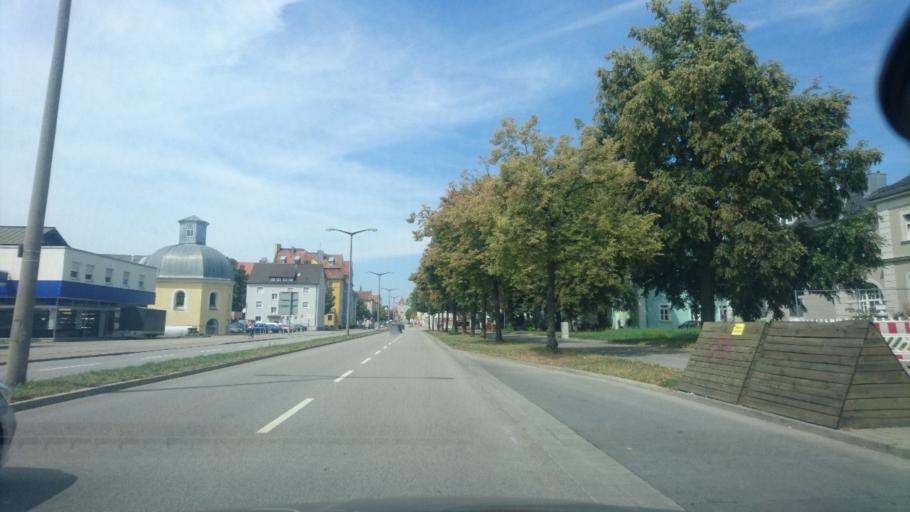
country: DE
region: Bavaria
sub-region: Upper Palatinate
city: Regensburg
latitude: 49.0156
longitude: 12.1181
